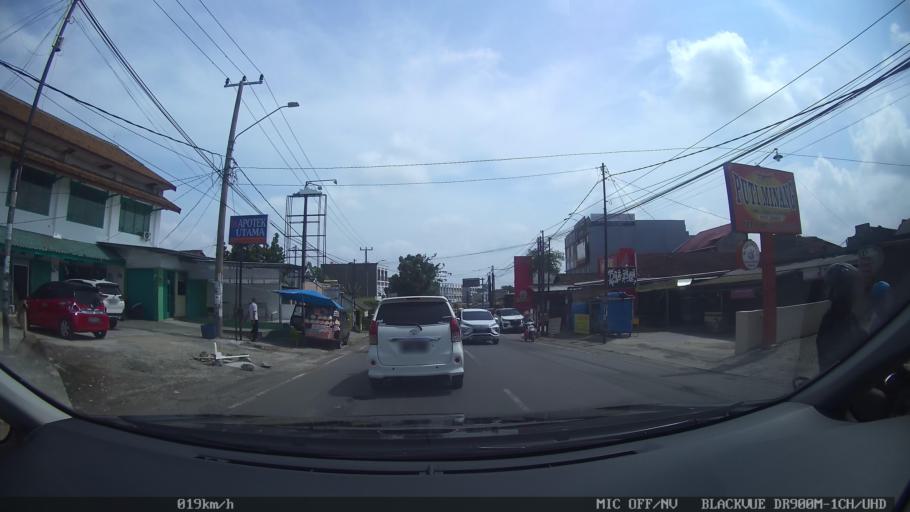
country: ID
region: Lampung
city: Kedaton
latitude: -5.3683
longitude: 105.2737
